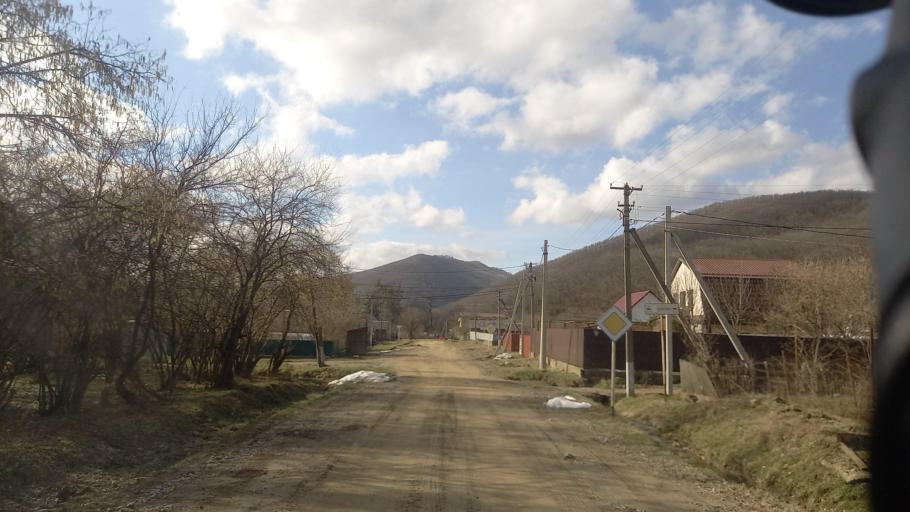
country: RU
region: Krasnodarskiy
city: Smolenskaya
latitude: 44.6047
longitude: 38.8515
